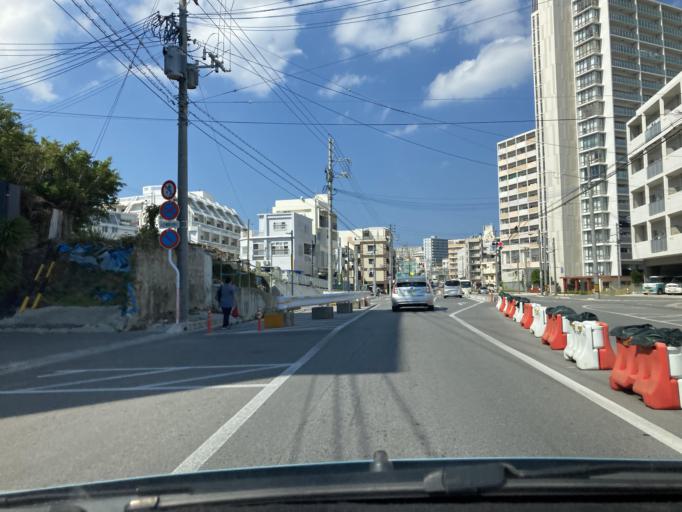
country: JP
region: Okinawa
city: Naha-shi
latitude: 26.2087
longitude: 127.6900
